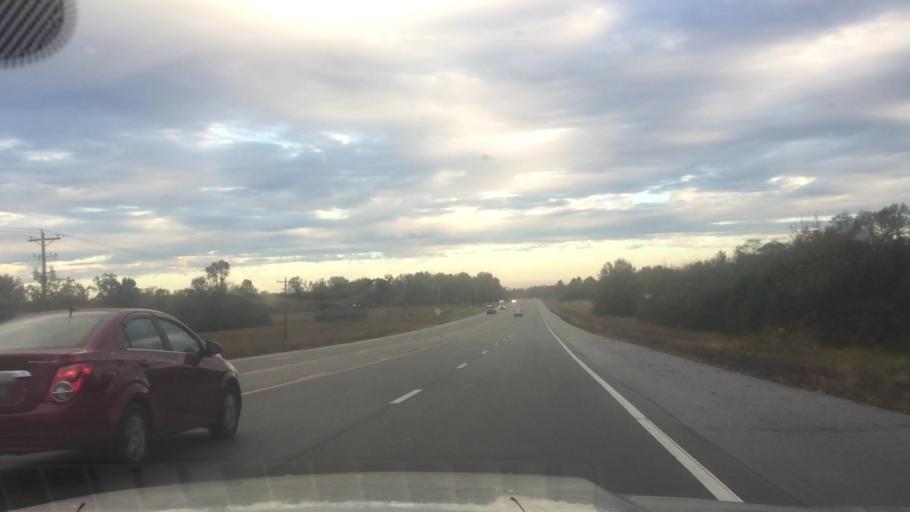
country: US
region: Tennessee
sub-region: Franklin County
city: Decherd
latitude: 35.2286
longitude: -86.1069
